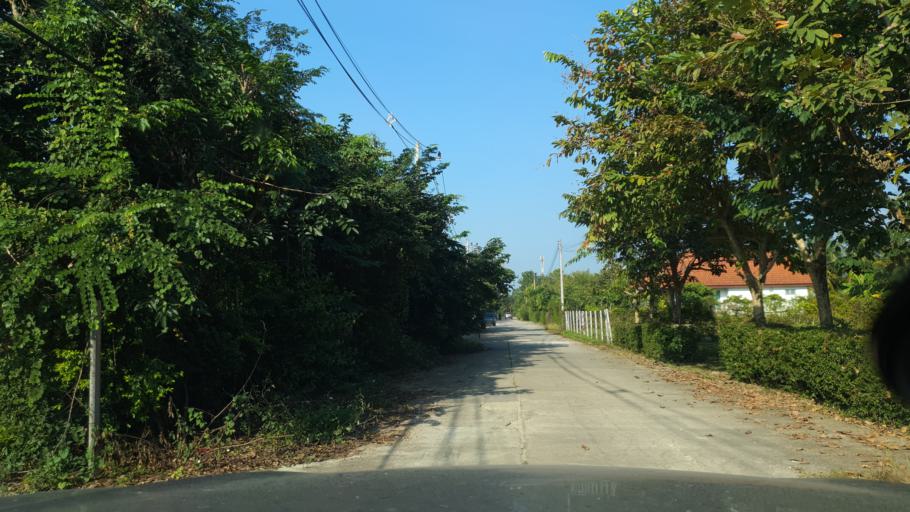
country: TH
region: Chiang Mai
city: Saraphi
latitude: 18.7136
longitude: 98.9946
